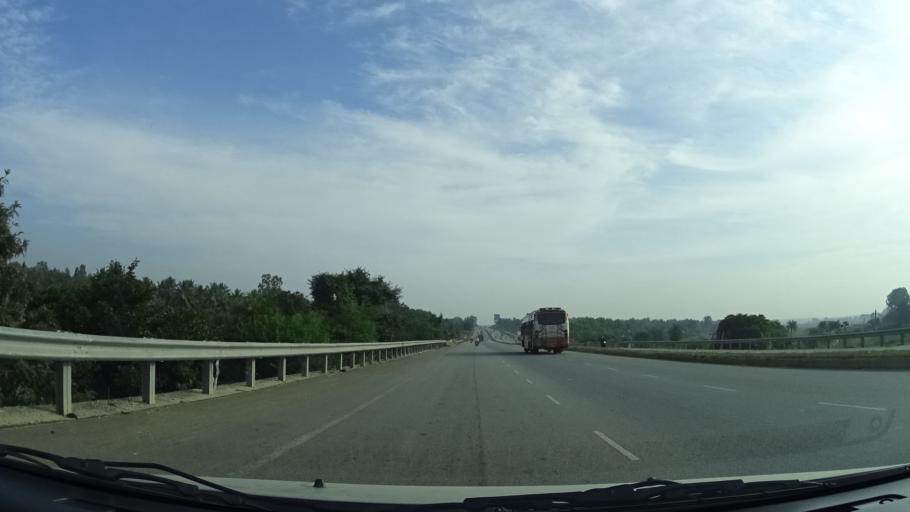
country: IN
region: Karnataka
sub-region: Bangalore Rural
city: Devanhalli
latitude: 13.2190
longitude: 77.6801
